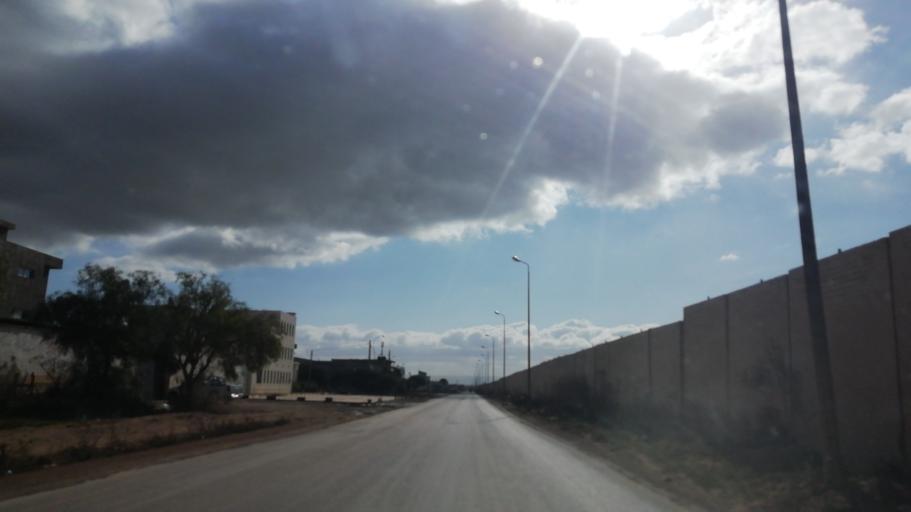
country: DZ
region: Oran
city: Es Senia
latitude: 35.6399
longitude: -0.6002
